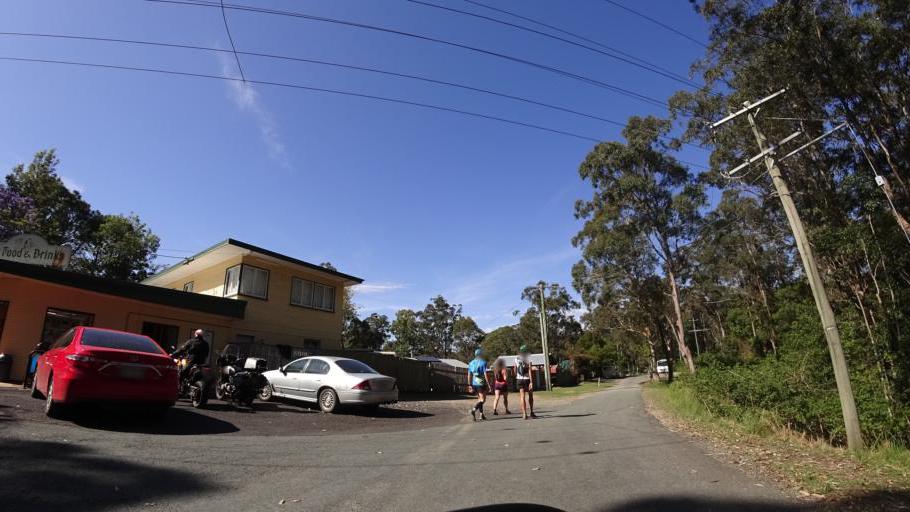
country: AU
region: Queensland
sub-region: Moreton Bay
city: Highvale
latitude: -27.3985
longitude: 152.7838
